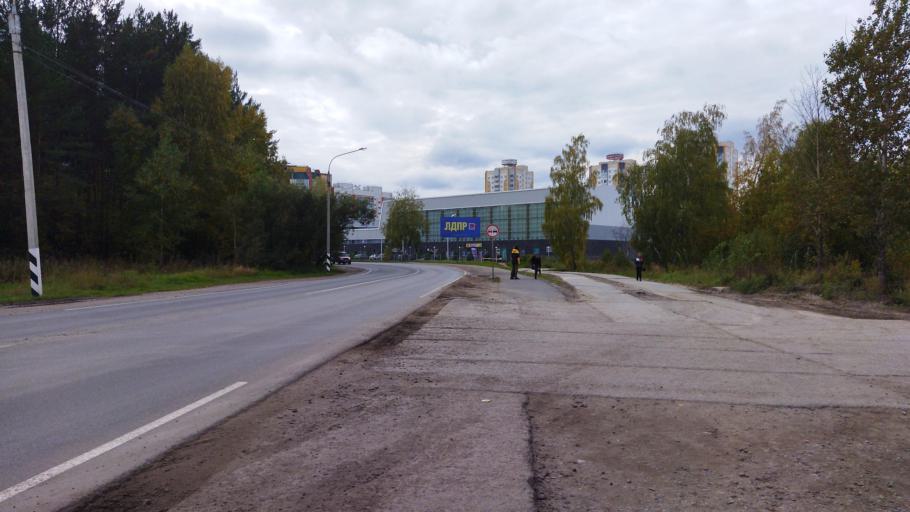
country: RU
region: Tomsk
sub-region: Tomskiy Rayon
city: Tomsk
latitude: 56.4945
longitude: 85.0621
